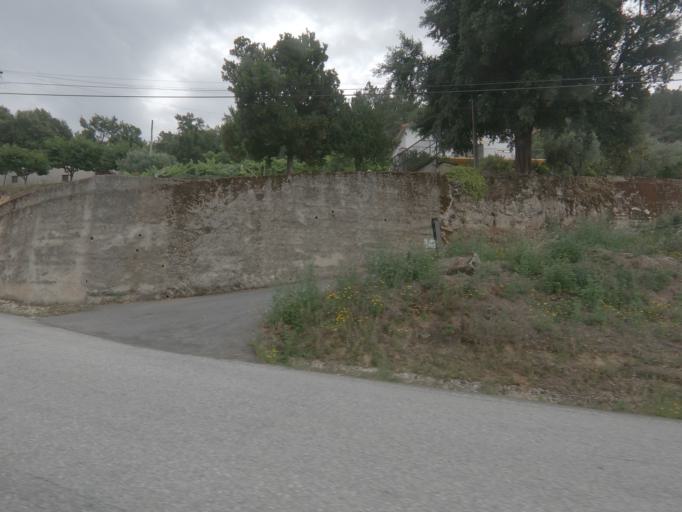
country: PT
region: Viseu
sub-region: Armamar
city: Armamar
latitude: 41.1199
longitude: -7.6676
